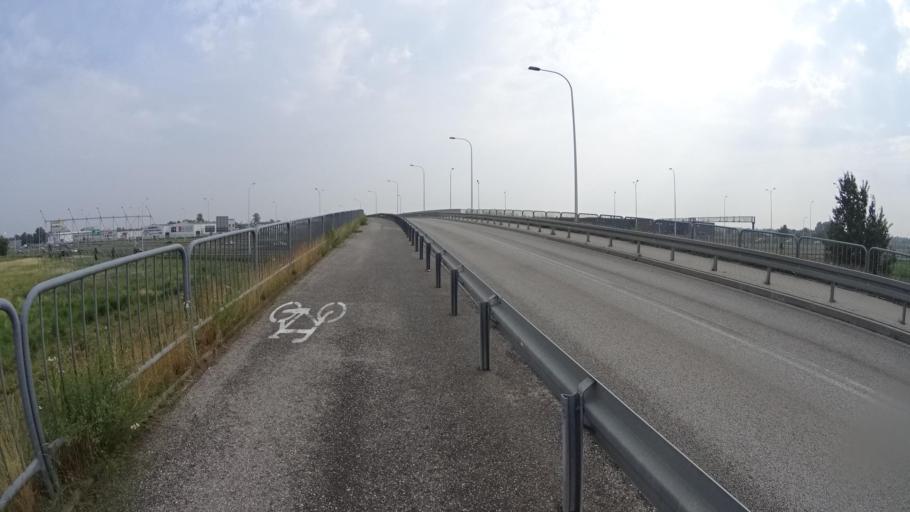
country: PL
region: Masovian Voivodeship
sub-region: Powiat pruszkowski
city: Nowe Grocholice
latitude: 52.1724
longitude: 20.9189
